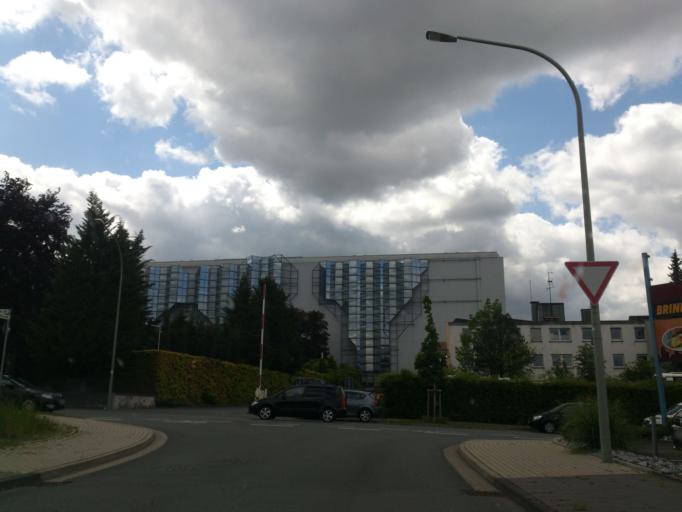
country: DE
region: North Rhine-Westphalia
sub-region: Regierungsbezirk Detmold
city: Paderborn
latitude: 51.7040
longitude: 8.7370
